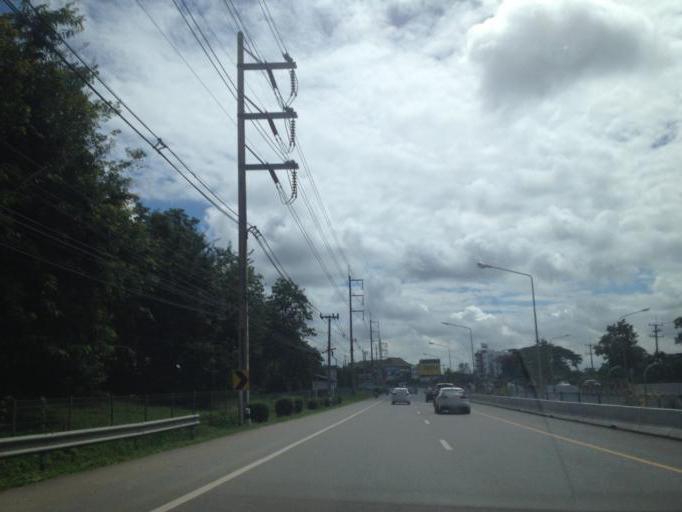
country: TH
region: Chiang Mai
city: Chiang Mai
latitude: 18.7778
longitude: 98.9542
